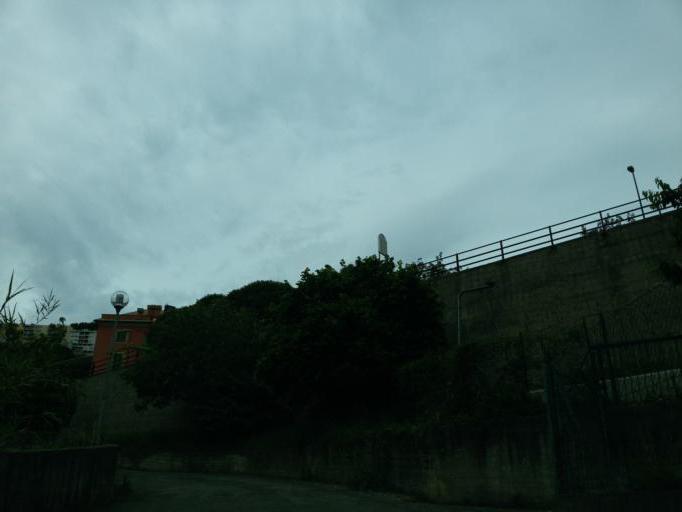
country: IT
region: Liguria
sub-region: Provincia di Genova
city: Piccarello
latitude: 44.4389
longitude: 8.9810
